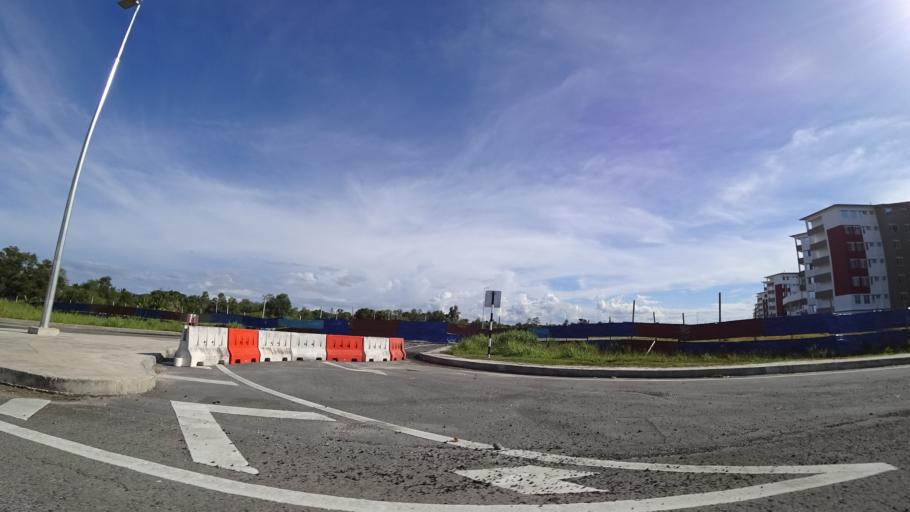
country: BN
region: Brunei and Muara
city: Bandar Seri Begawan
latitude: 4.9757
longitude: 114.9765
